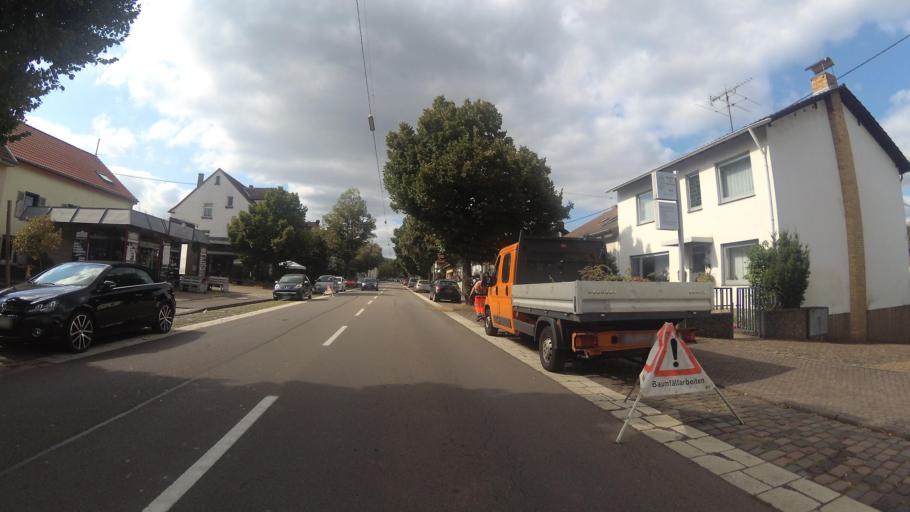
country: DE
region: Saarland
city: Wadgassen
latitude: 49.2675
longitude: 6.7952
